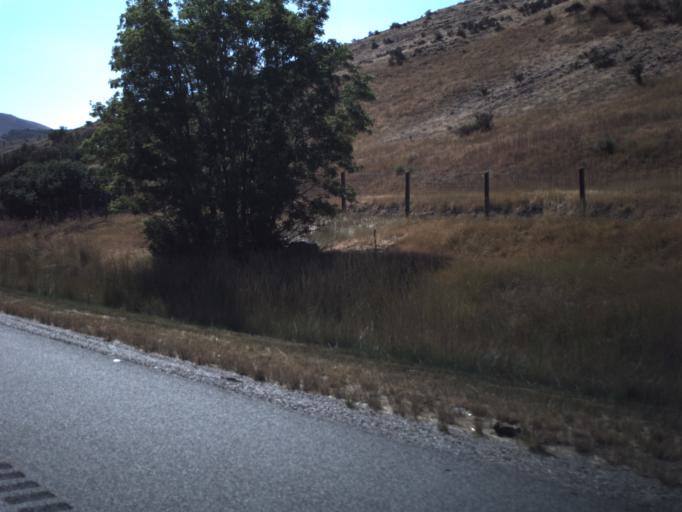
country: US
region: Utah
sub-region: Box Elder County
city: Brigham City
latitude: 41.5131
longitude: -111.9428
